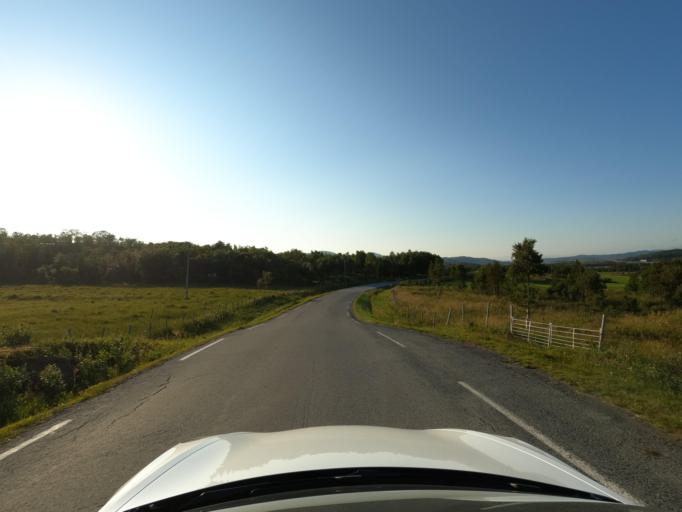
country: NO
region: Troms
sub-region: Skanland
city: Evenskjer
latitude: 68.4596
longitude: 16.6811
